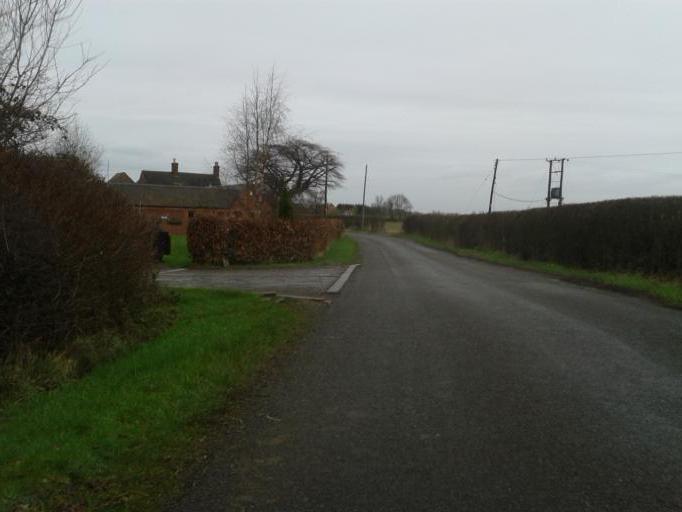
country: GB
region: England
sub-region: Warwickshire
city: Atherstone
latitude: 52.5965
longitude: -1.5287
